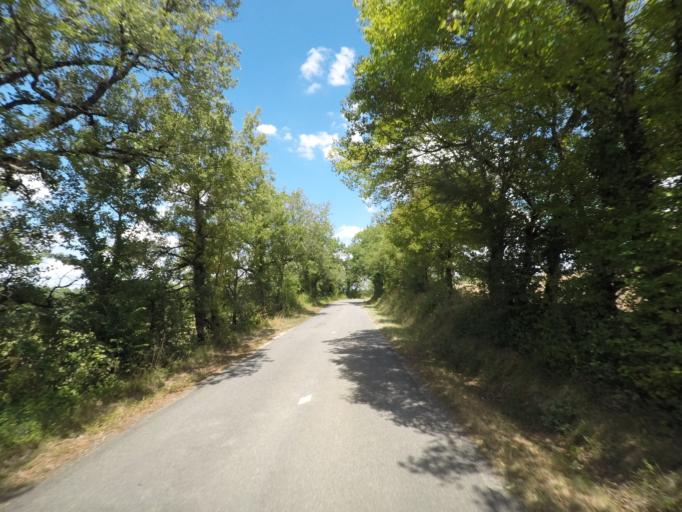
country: FR
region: Midi-Pyrenees
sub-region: Departement du Lot
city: Le Vigan
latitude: 44.6156
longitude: 1.5942
